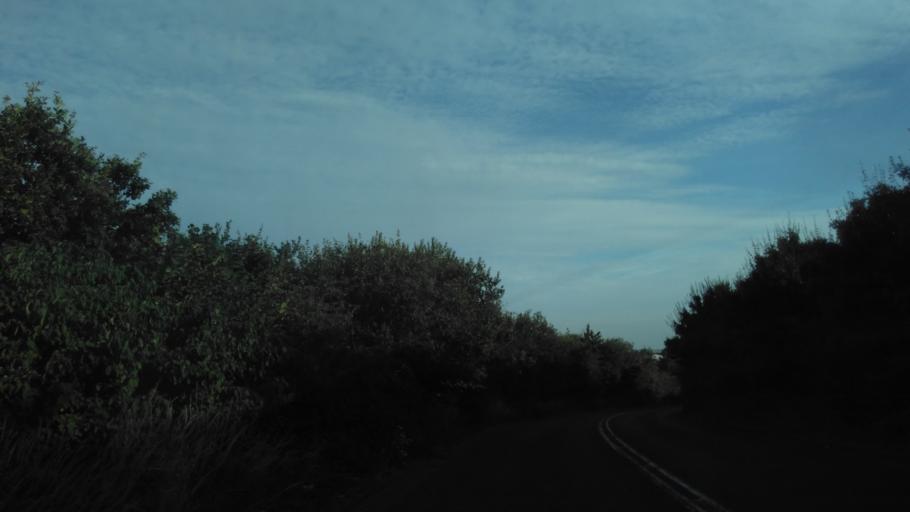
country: GB
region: England
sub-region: Kent
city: Dunkirk
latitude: 51.3245
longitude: 0.9833
